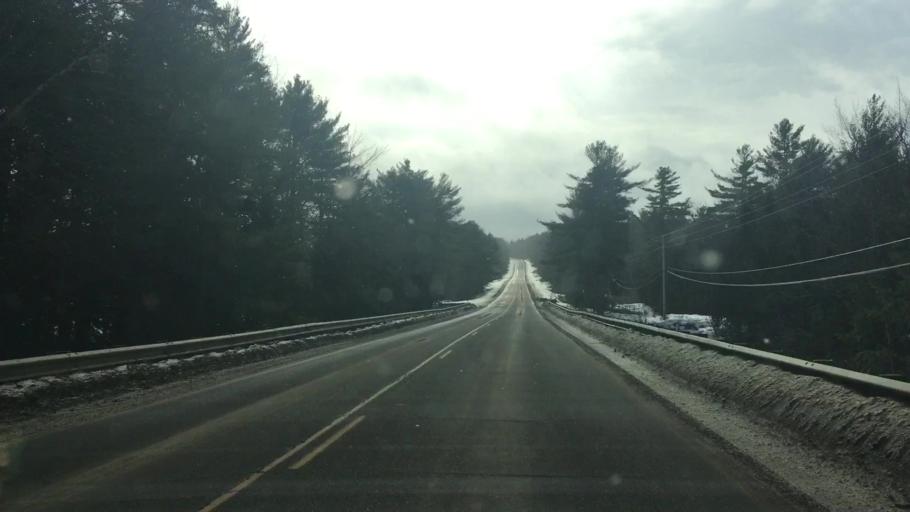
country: US
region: Maine
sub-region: Washington County
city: Calais
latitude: 45.0746
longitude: -67.3322
